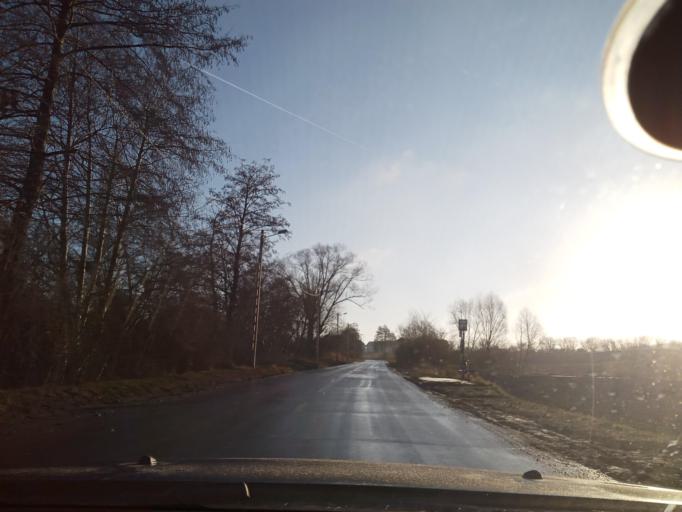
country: PL
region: Lesser Poland Voivodeship
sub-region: Powiat krakowski
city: Michalowice
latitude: 50.1058
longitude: 20.0493
